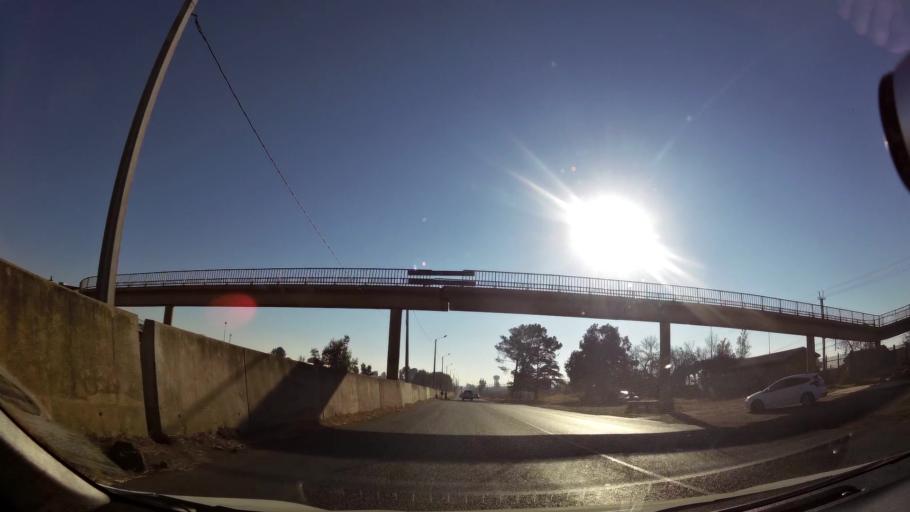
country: ZA
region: Gauteng
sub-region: Ekurhuleni Metropolitan Municipality
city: Germiston
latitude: -26.3507
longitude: 28.1255
